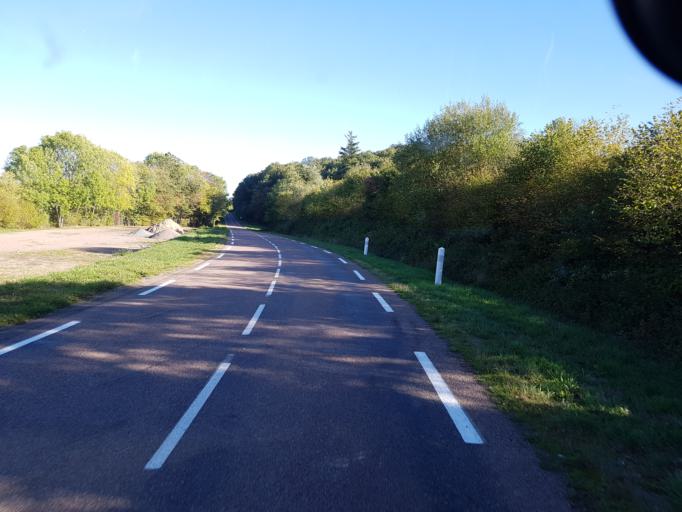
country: FR
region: Bourgogne
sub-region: Departement de Saone-et-Loire
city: Autun
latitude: 47.0486
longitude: 4.2684
